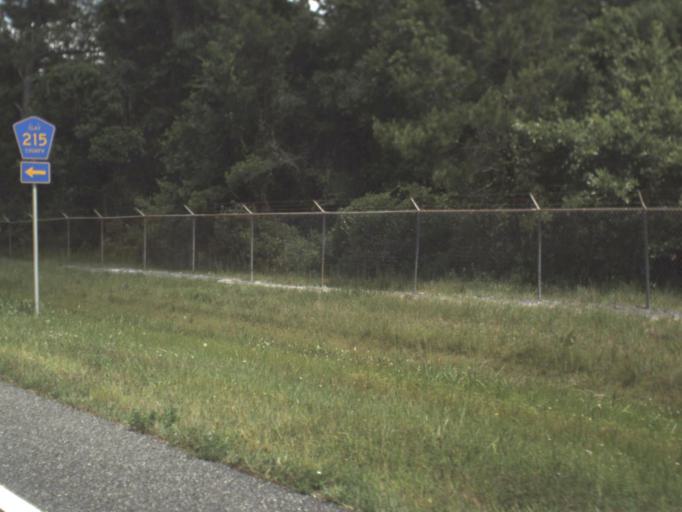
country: US
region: Florida
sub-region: Bradford County
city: Starke
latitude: 29.9815
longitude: -81.9756
